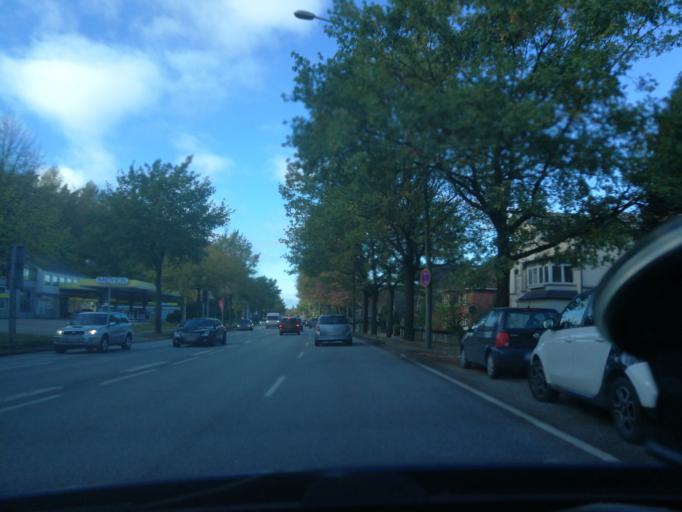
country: DE
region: Hamburg
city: Altona
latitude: 53.4715
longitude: 9.8982
